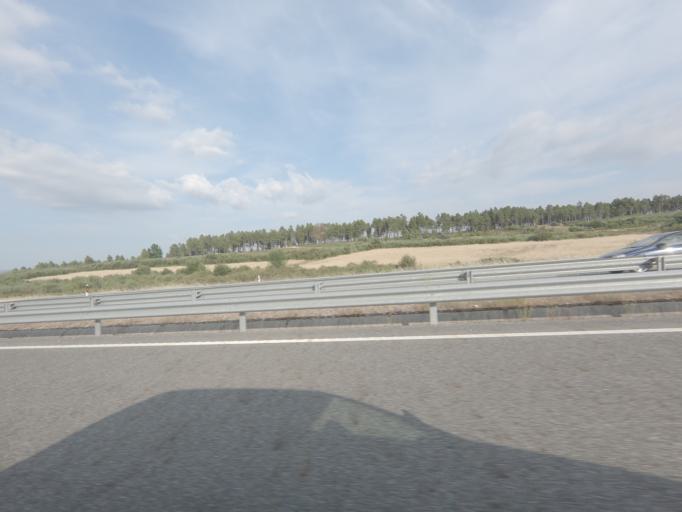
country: PT
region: Vila Real
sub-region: Chaves
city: Chaves
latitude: 41.7553
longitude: -7.5155
